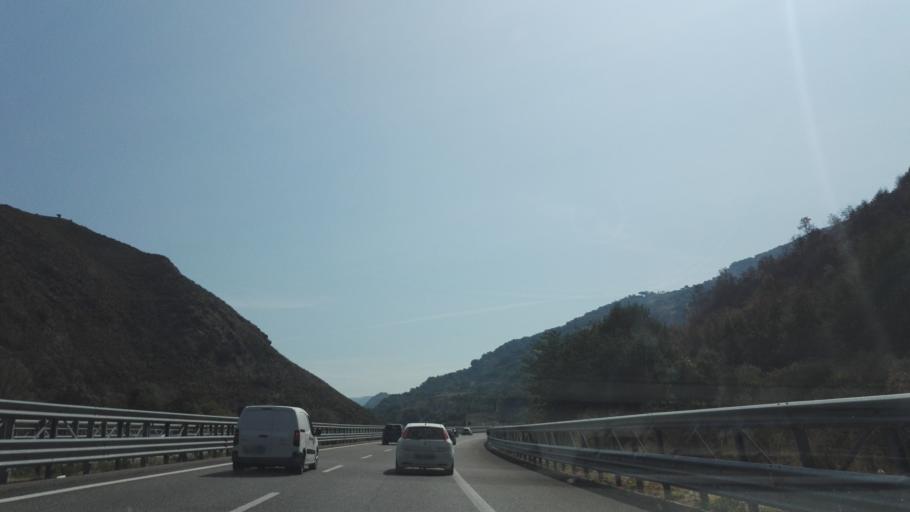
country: IT
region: Calabria
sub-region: Provincia di Catanzaro
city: San Mango d'Aquino
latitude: 39.0806
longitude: 16.1991
